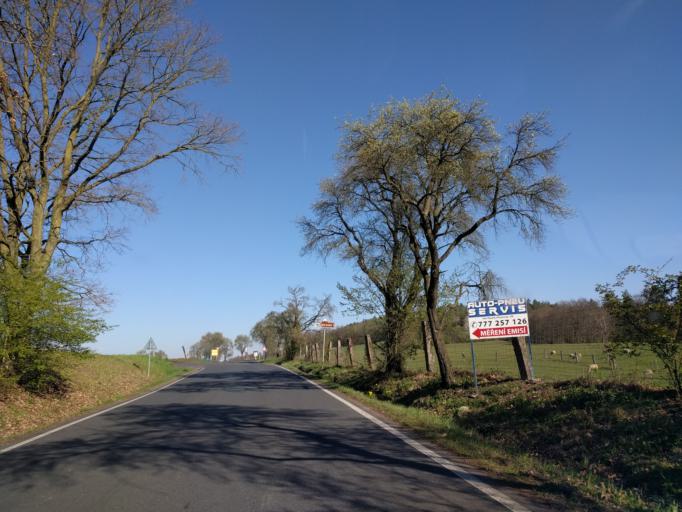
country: CZ
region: Central Bohemia
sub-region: Okres Praha-Vychod
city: Mnichovice
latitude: 49.9201
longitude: 14.7399
